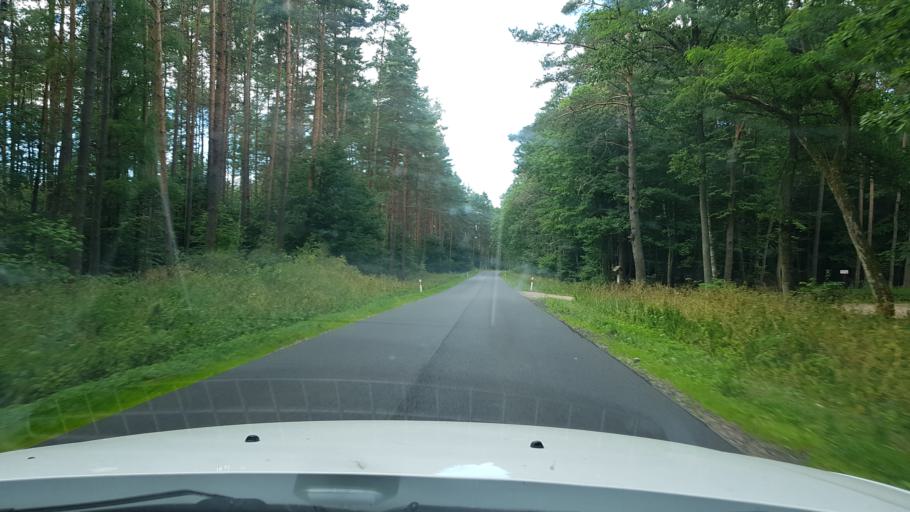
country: PL
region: West Pomeranian Voivodeship
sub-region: Powiat drawski
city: Zlocieniec
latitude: 53.5072
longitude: 16.0254
